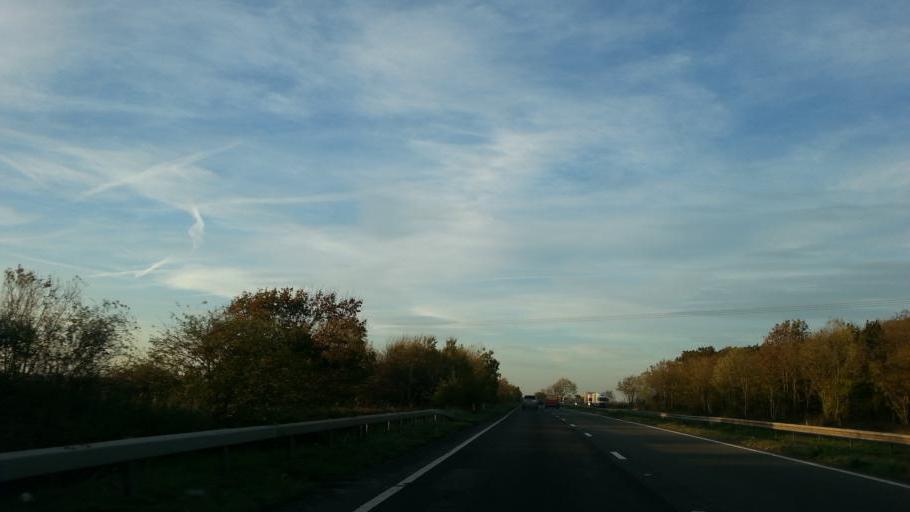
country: GB
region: England
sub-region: District of Rutland
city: Greetham
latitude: 52.7499
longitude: -0.6055
